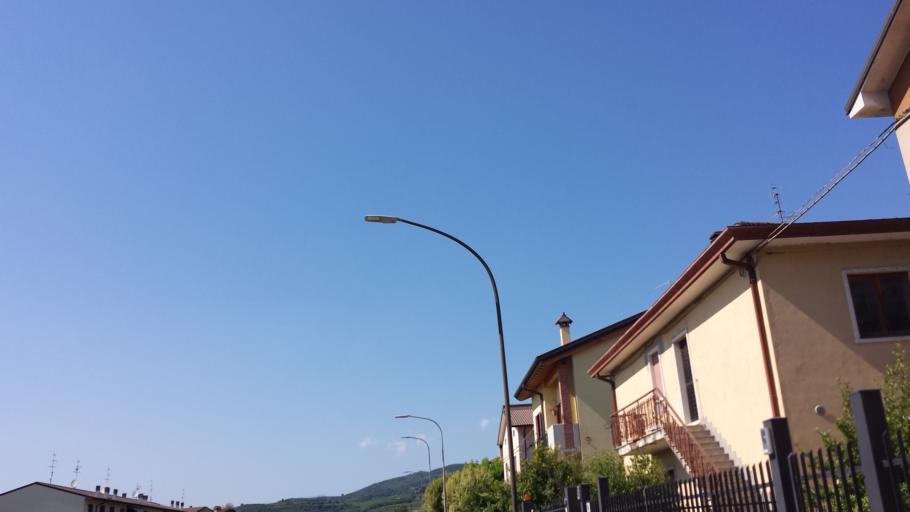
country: IT
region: Veneto
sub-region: Provincia di Verona
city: Soave
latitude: 45.4255
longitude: 11.2454
